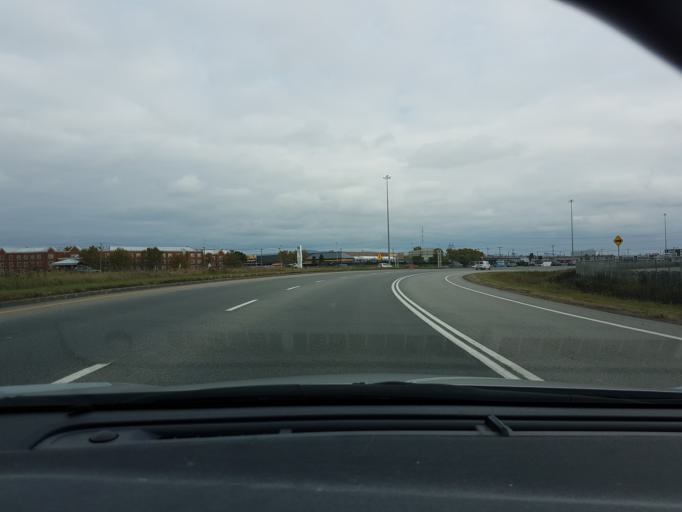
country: CA
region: Quebec
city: L'Ancienne-Lorette
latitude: 46.8246
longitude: -71.2944
